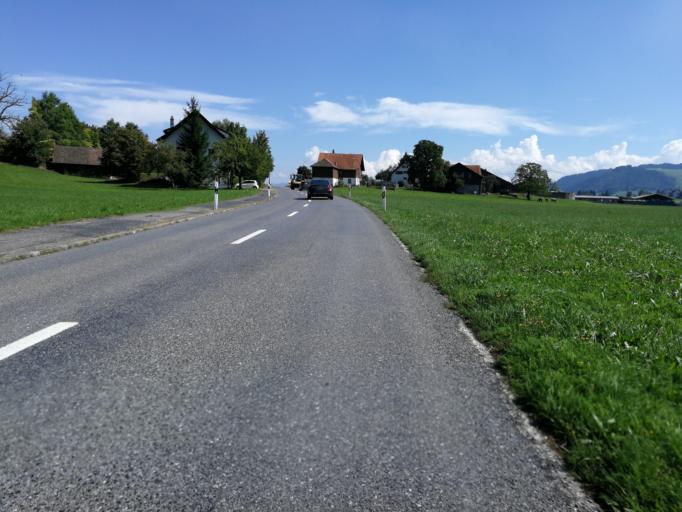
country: CH
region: Zurich
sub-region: Bezirk Horgen
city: Waedenswil / Untermosen-Fuhr
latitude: 47.2116
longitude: 8.6496
